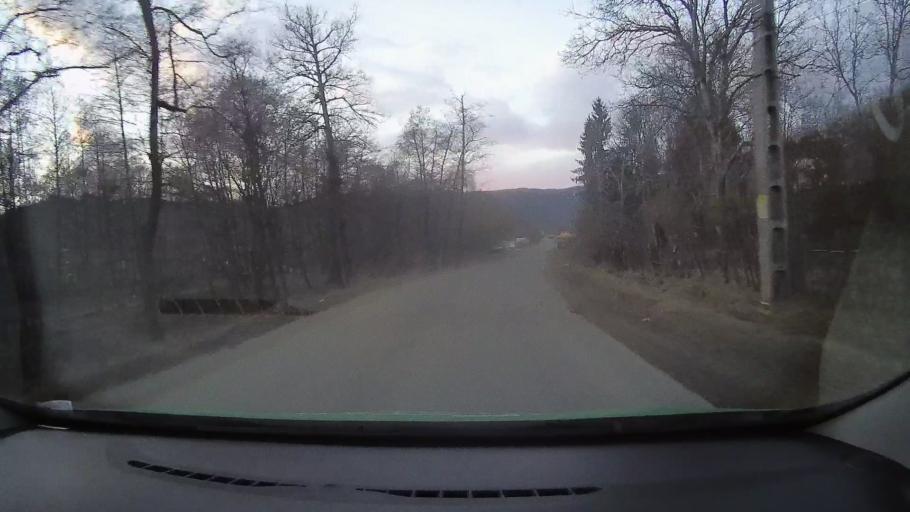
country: RO
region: Dambovita
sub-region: Comuna Valea Lunga
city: Valea Lunga-Cricov
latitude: 45.0705
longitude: 25.5797
